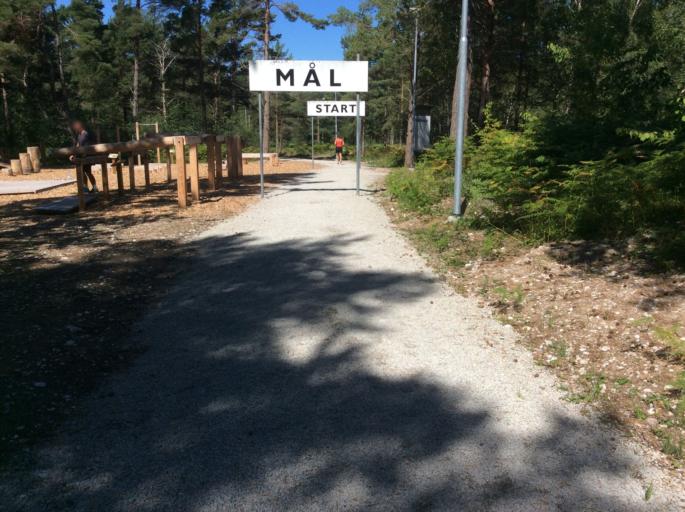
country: SE
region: Gotland
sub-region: Gotland
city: Vibble
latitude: 57.6053
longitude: 18.2798
